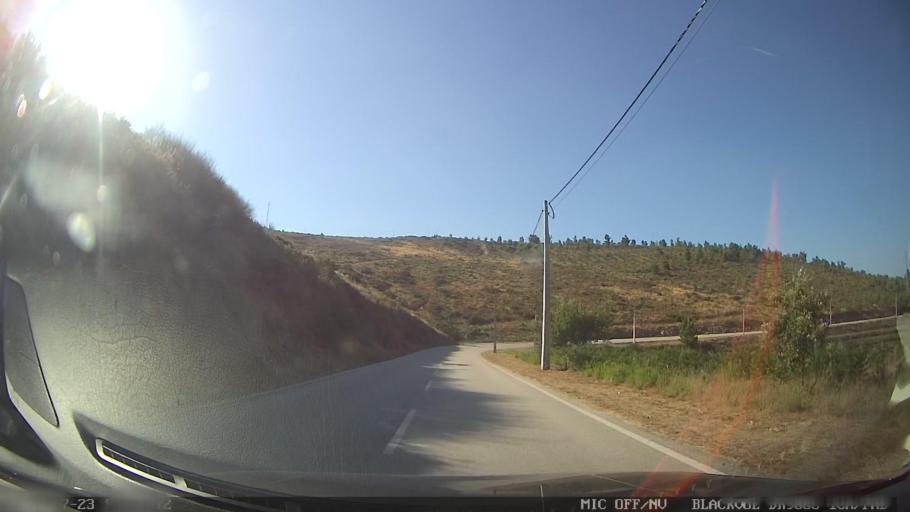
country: PT
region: Viseu
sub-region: Sao Joao da Pesqueira
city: Sao Joao da Pesqueira
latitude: 41.1595
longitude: -7.4364
